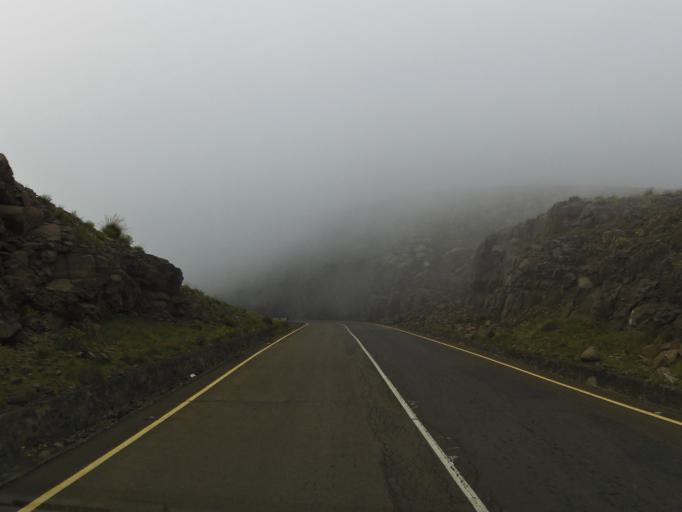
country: LS
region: Butha-Buthe
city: Butha-Buthe
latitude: -29.0640
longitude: 28.4060
